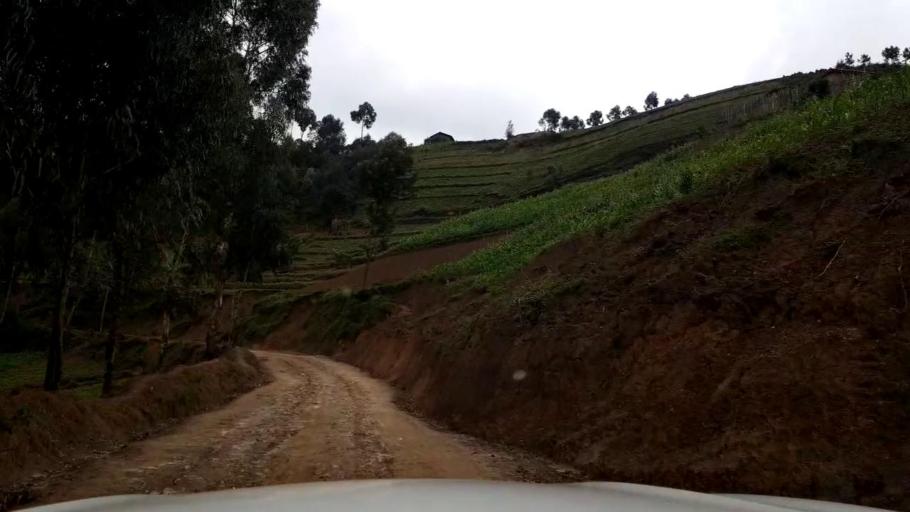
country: RW
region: Western Province
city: Kibuye
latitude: -1.9664
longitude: 29.4846
